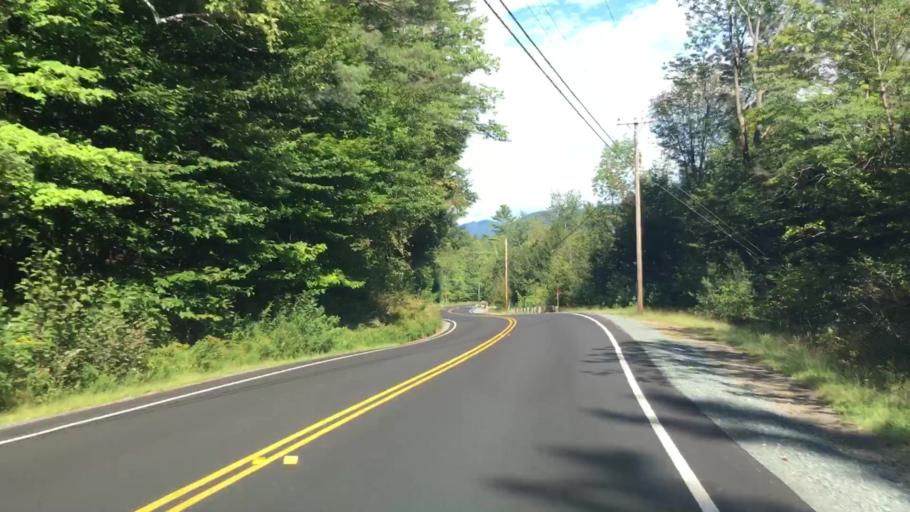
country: US
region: New Hampshire
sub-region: Grafton County
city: Woodstock
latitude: 44.0281
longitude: -71.7212
